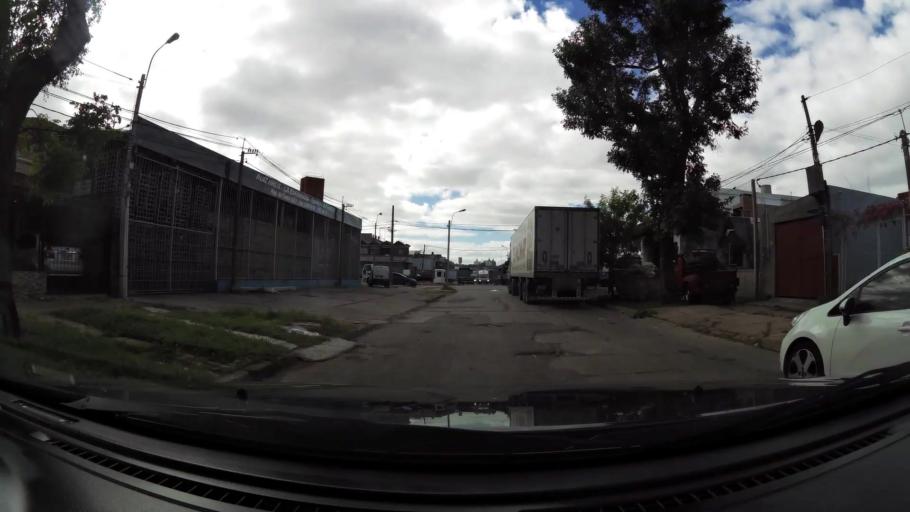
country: UY
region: Montevideo
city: Montevideo
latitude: -34.8713
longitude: -56.1565
